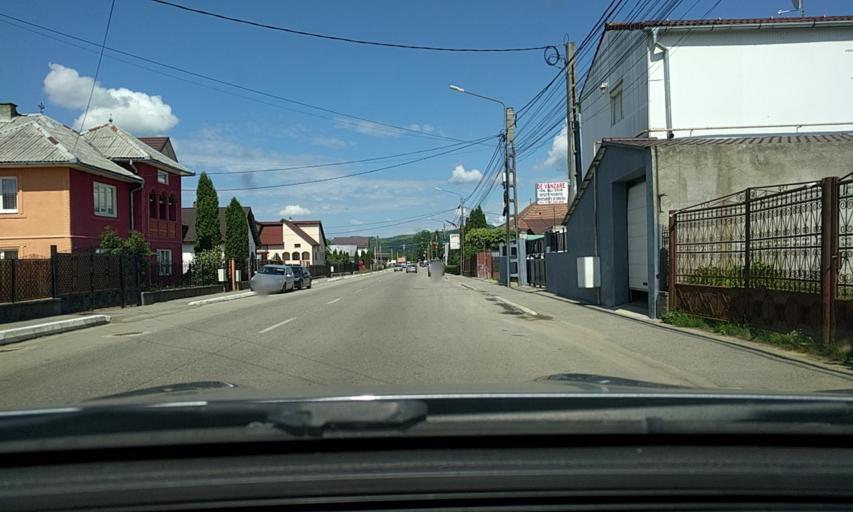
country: RO
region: Bistrita-Nasaud
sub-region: Oras Nasaud
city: Nasaud
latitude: 47.2944
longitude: 24.3842
